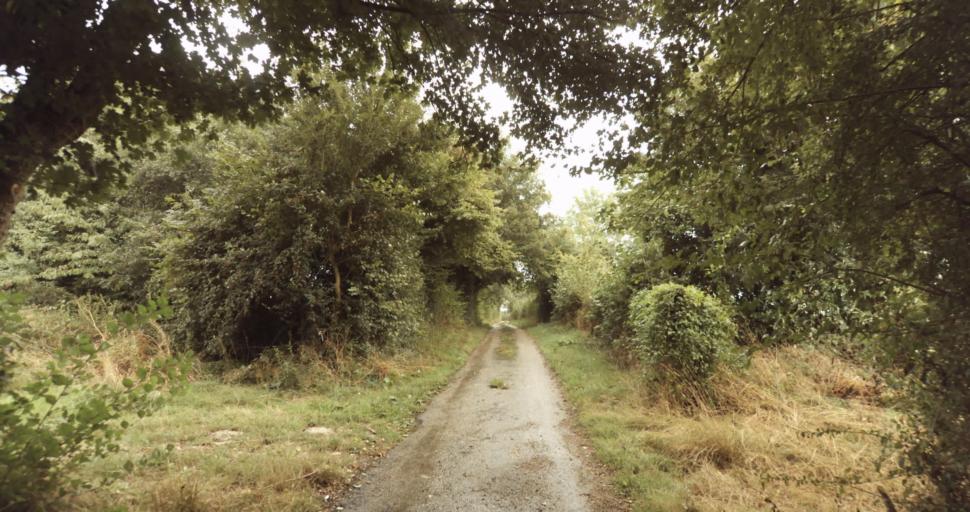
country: FR
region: Lower Normandy
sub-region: Departement de l'Orne
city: Vimoutiers
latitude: 48.8771
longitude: 0.1853
